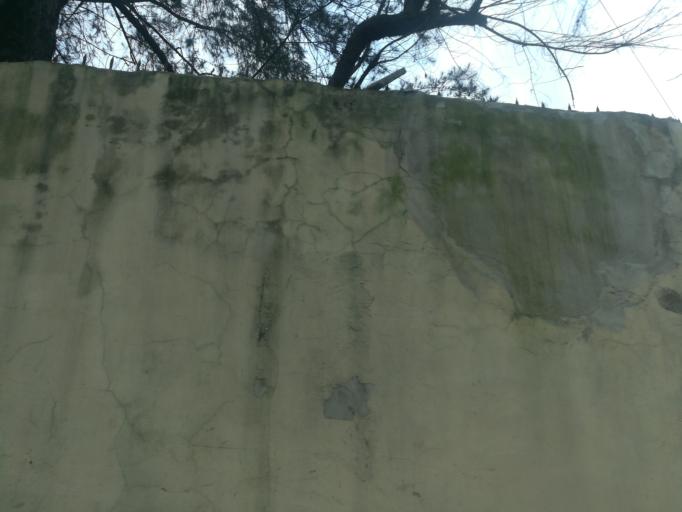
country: NG
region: Lagos
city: Ojota
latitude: 6.5662
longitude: 3.3655
